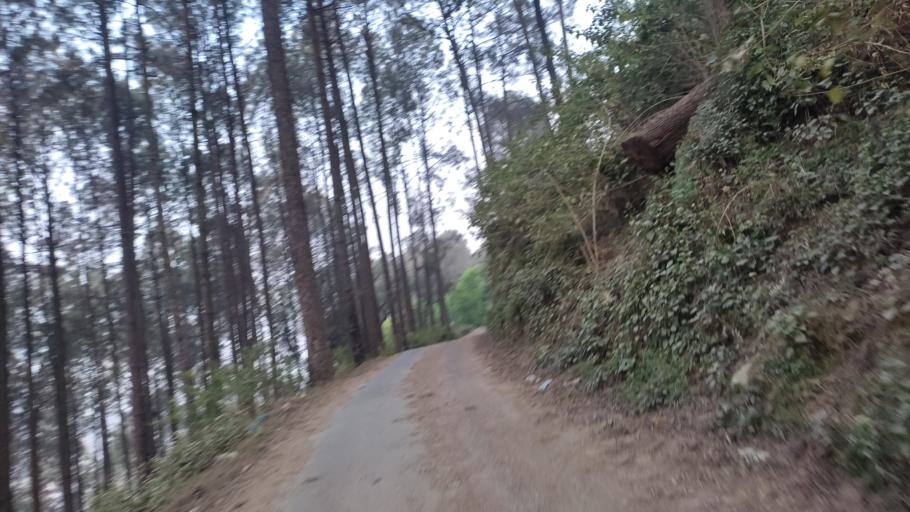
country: NP
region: Central Region
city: Kirtipur
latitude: 27.6681
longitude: 85.2920
